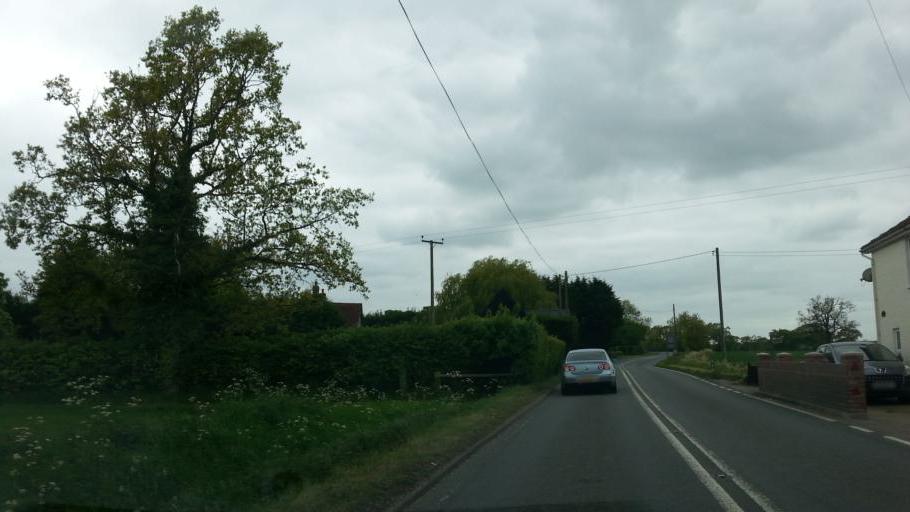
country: GB
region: England
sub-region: Suffolk
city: Capel Saint Mary
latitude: 52.0566
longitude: 1.0193
